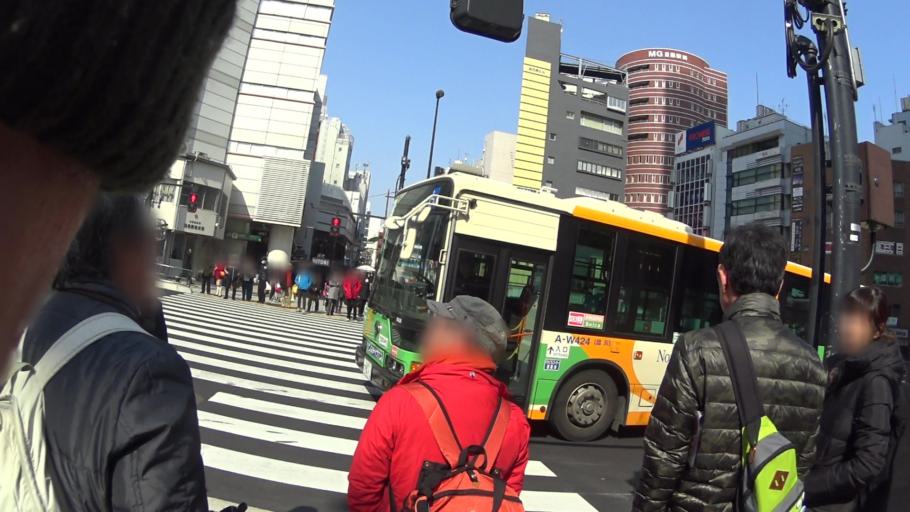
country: JP
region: Tokyo
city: Tokyo
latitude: 35.6336
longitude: 139.7162
